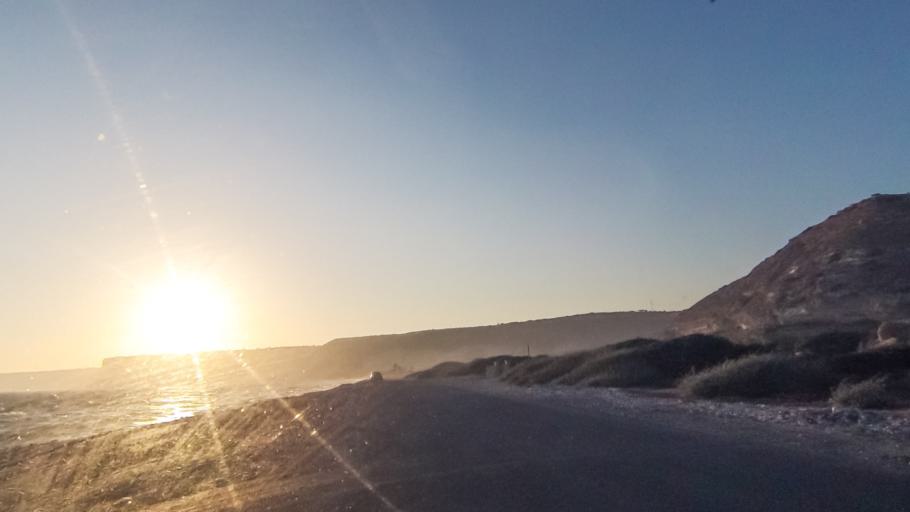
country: CY
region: Limassol
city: Erimi
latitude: 34.6598
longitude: 32.8853
